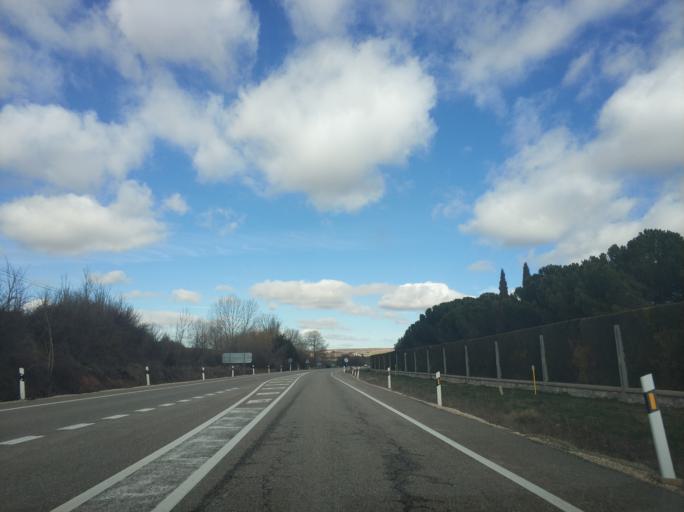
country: ES
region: Castille and Leon
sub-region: Provincia de Burgos
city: Sarracin
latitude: 42.2536
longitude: -3.6889
